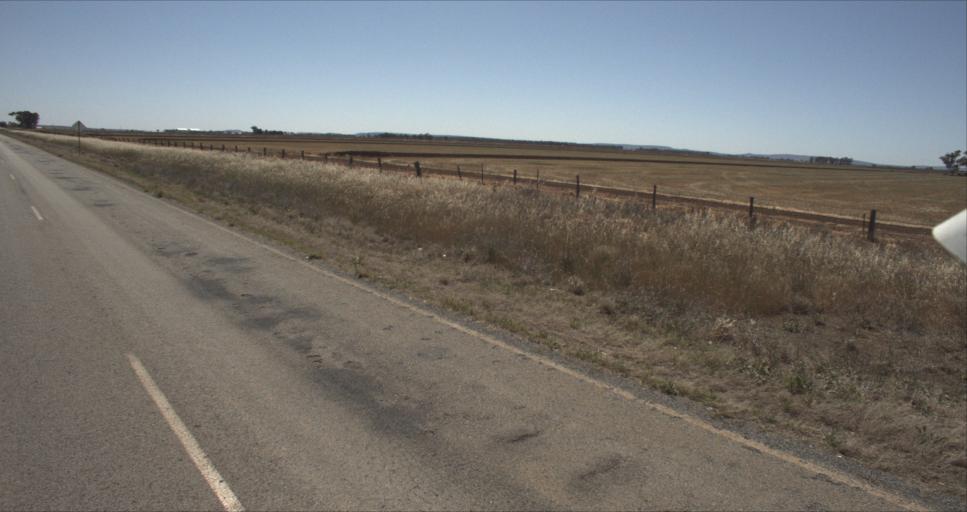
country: AU
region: New South Wales
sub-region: Leeton
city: Leeton
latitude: -34.5172
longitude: 146.2840
